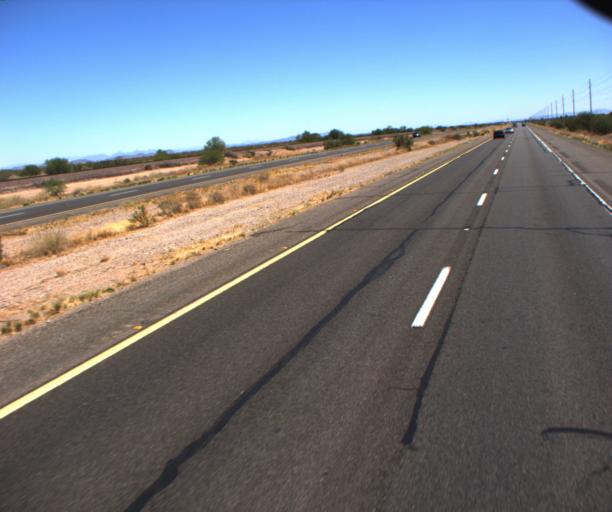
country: US
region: Arizona
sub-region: Maricopa County
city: Sun City West
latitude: 33.7239
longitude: -112.4597
